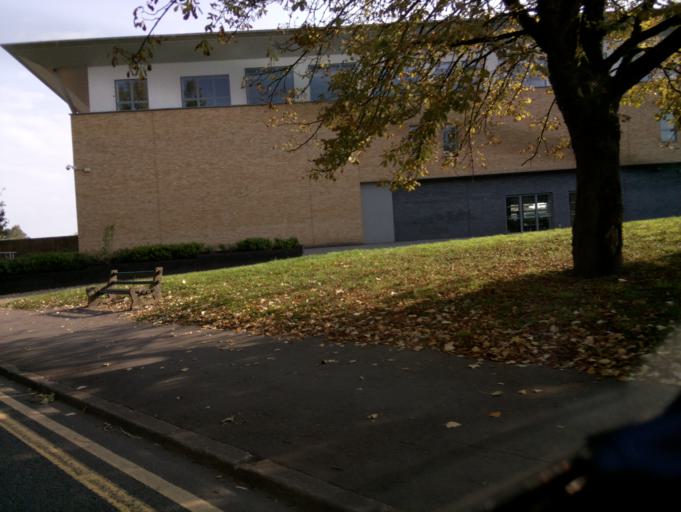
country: GB
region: Wales
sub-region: Newport
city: Newport
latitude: 51.6075
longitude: -3.0144
